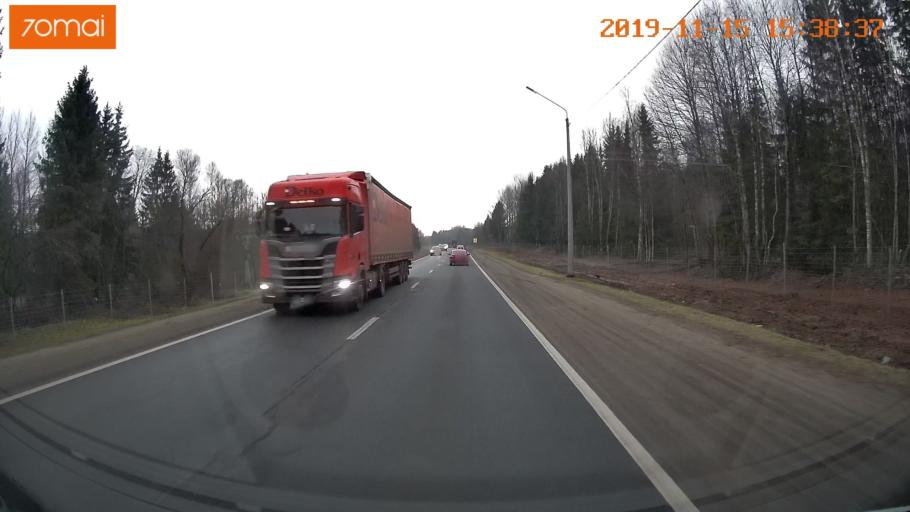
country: RU
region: Jaroslavl
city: Danilov
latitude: 58.0284
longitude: 40.0784
